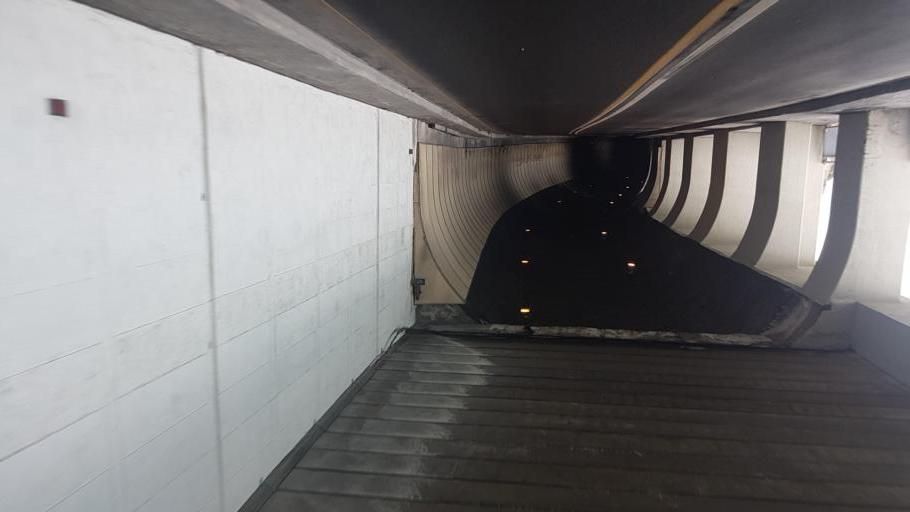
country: IT
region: Liguria
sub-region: Provincia di Genova
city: Sestri Levante
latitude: 44.2830
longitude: 9.3880
